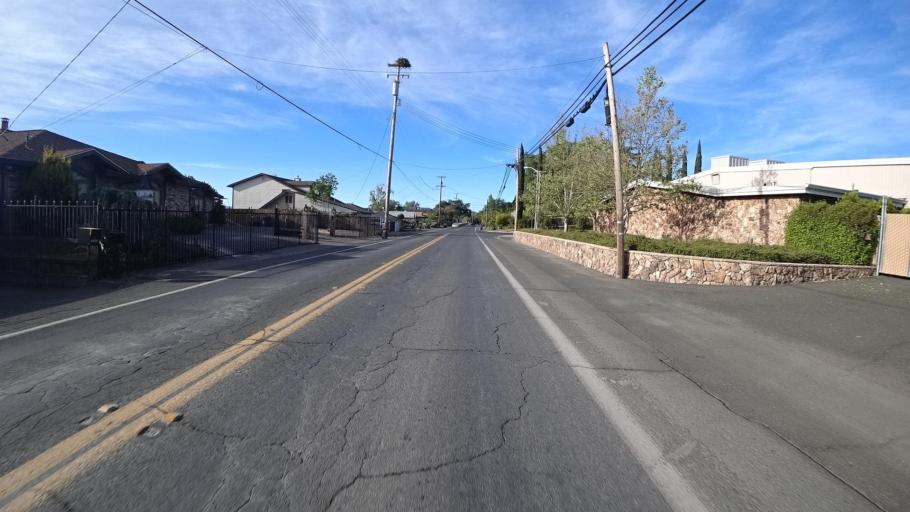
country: US
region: California
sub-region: Lake County
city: North Lakeport
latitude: 39.0681
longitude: -122.9130
